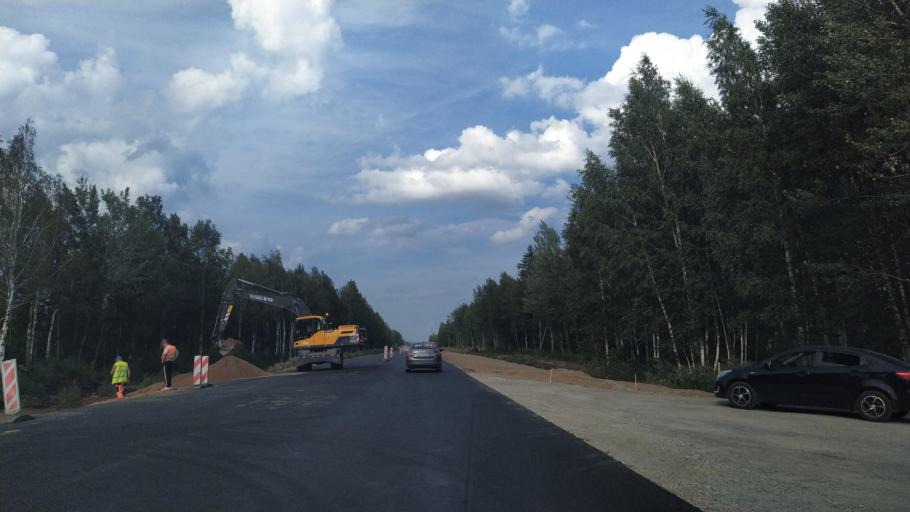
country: RU
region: Novgorod
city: Shimsk
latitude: 58.2955
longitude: 30.8674
